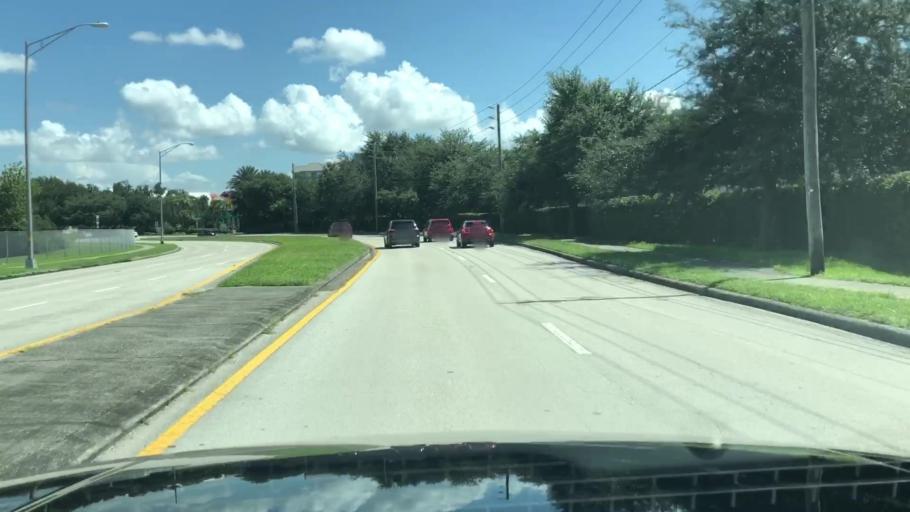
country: US
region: Florida
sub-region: Osceola County
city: Celebration
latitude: 28.3382
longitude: -81.4873
